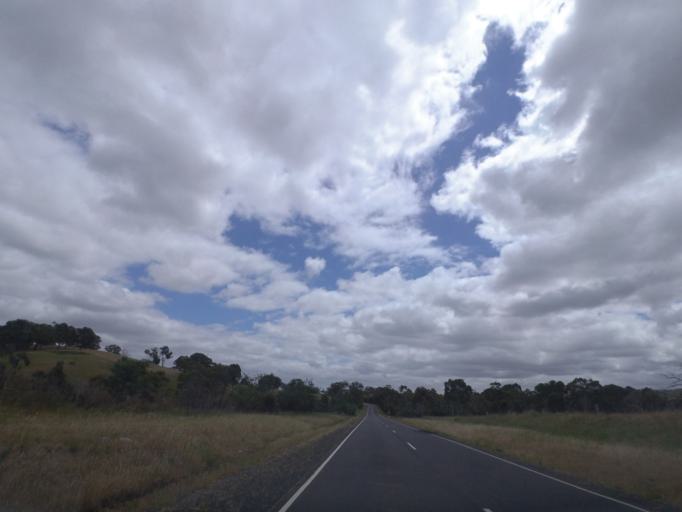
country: AU
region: Victoria
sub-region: Whittlesea
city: Whittlesea
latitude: -37.2769
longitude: 145.0510
